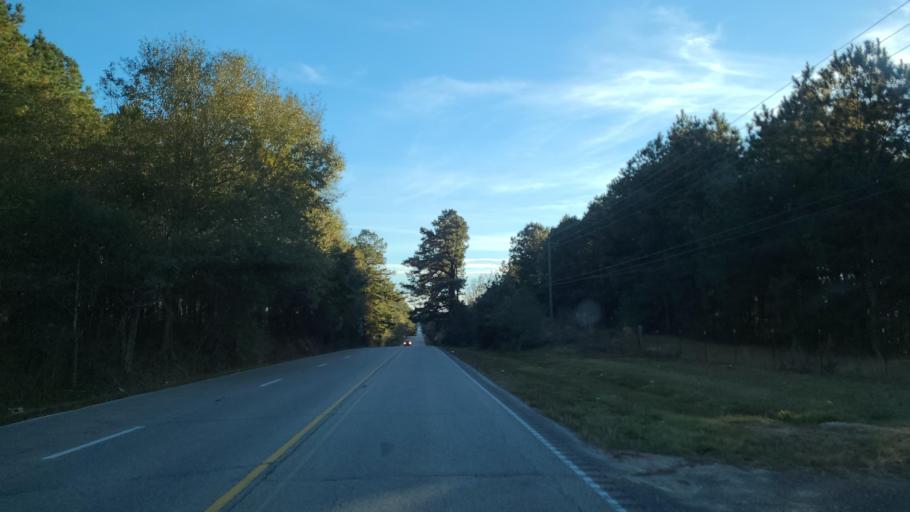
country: US
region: Mississippi
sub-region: Lamar County
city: Purvis
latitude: 31.0969
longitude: -89.4141
